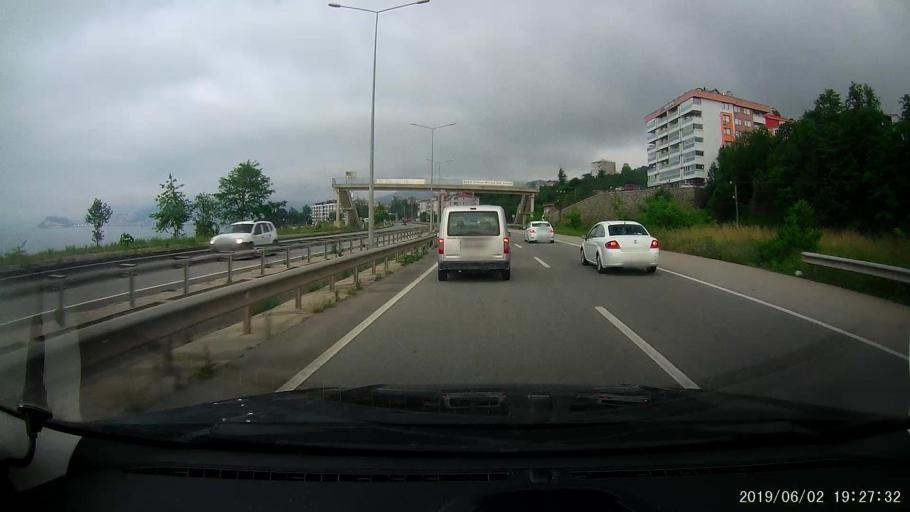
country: TR
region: Giresun
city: Bulancak
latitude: 40.9303
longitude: 38.3079
